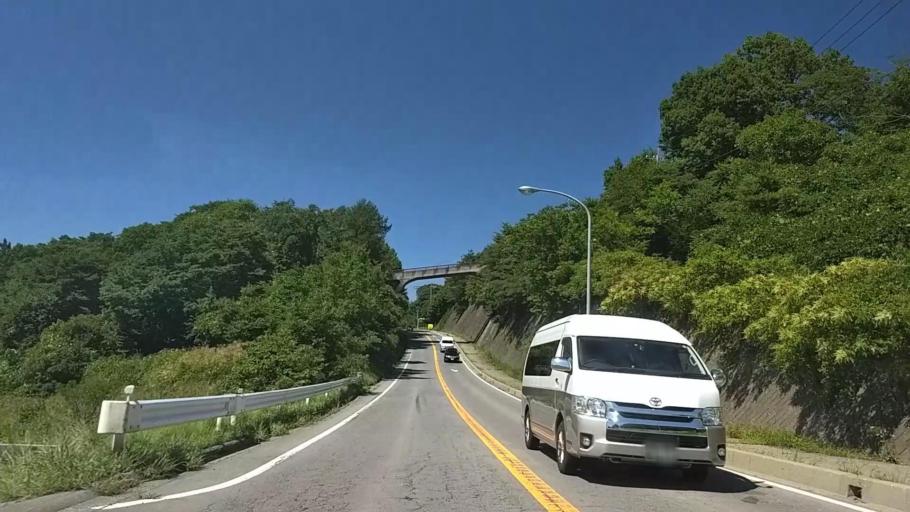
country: JP
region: Nagano
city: Komoro
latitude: 36.3517
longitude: 138.4136
